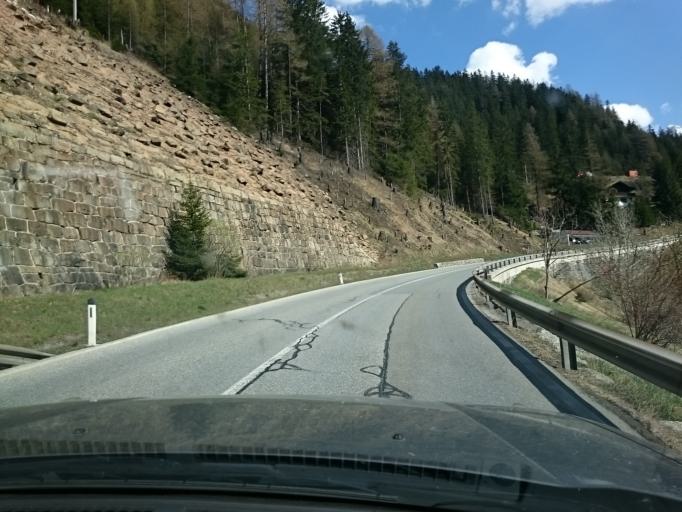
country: AT
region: Tyrol
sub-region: Politischer Bezirk Innsbruck Land
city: Gries am Brenner
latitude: 47.0270
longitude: 11.5012
